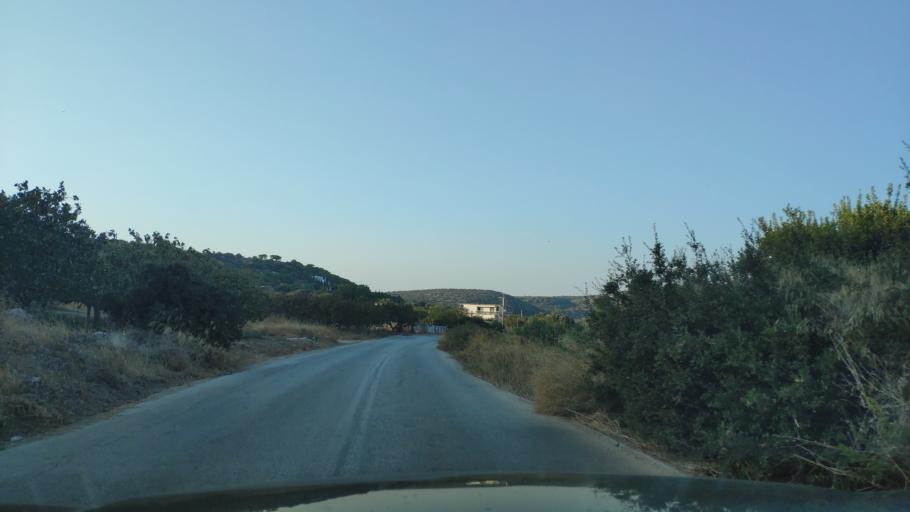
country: GR
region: Attica
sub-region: Nomarchia Anatolikis Attikis
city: Limin Mesoyaias
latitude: 37.9220
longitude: 23.9775
